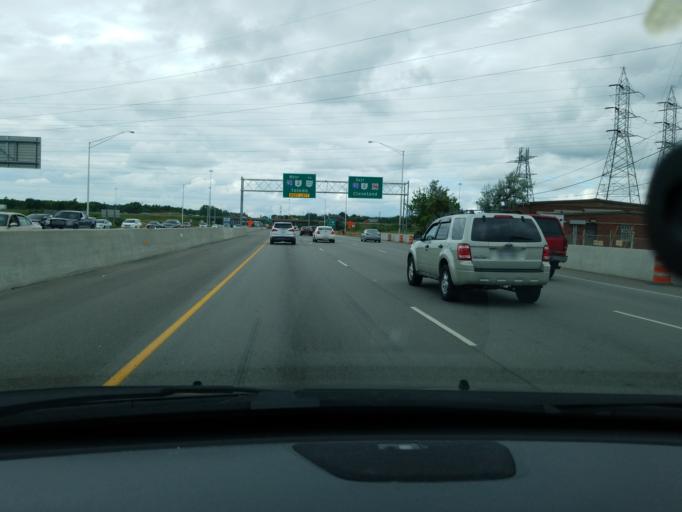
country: US
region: Ohio
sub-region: Lorain County
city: Sheffield
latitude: 41.4010
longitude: -82.1165
